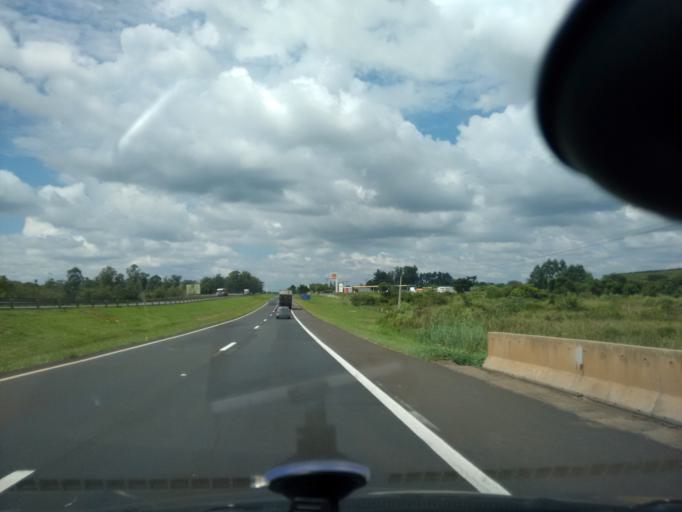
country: BR
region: Sao Paulo
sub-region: Sao Carlos
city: Sao Carlos
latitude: -22.0874
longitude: -47.8348
